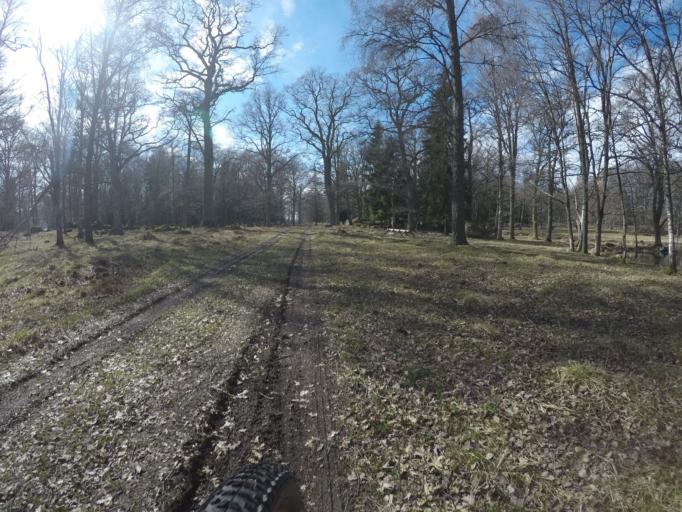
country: SE
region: Vaestmanland
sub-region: Kungsors Kommun
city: Kungsoer
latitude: 59.2732
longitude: 16.1394
